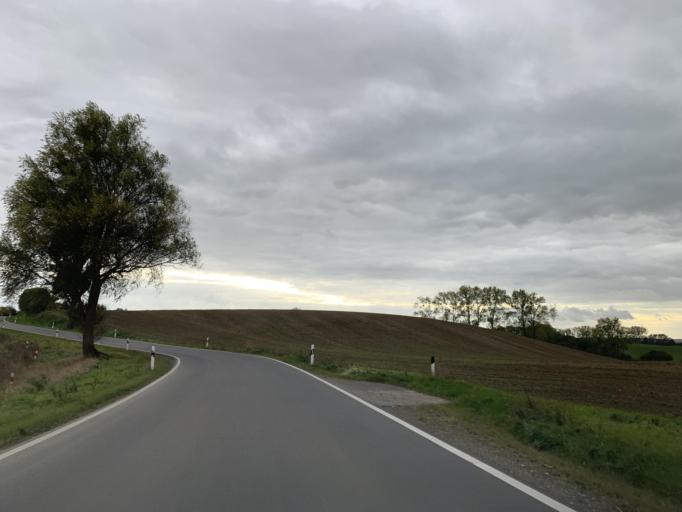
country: DE
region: Mecklenburg-Vorpommern
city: Burg Stargard
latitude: 53.4629
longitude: 13.2913
